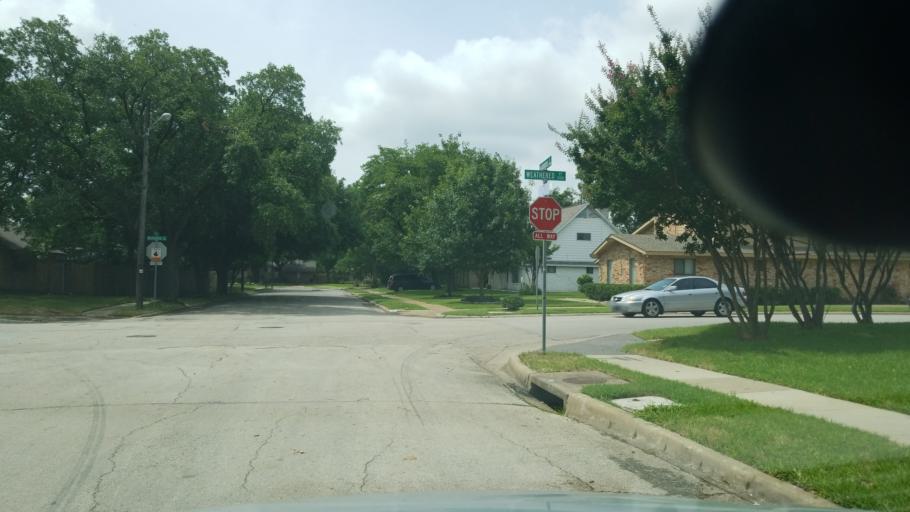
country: US
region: Texas
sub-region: Dallas County
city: Irving
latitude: 32.8401
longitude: -96.9629
